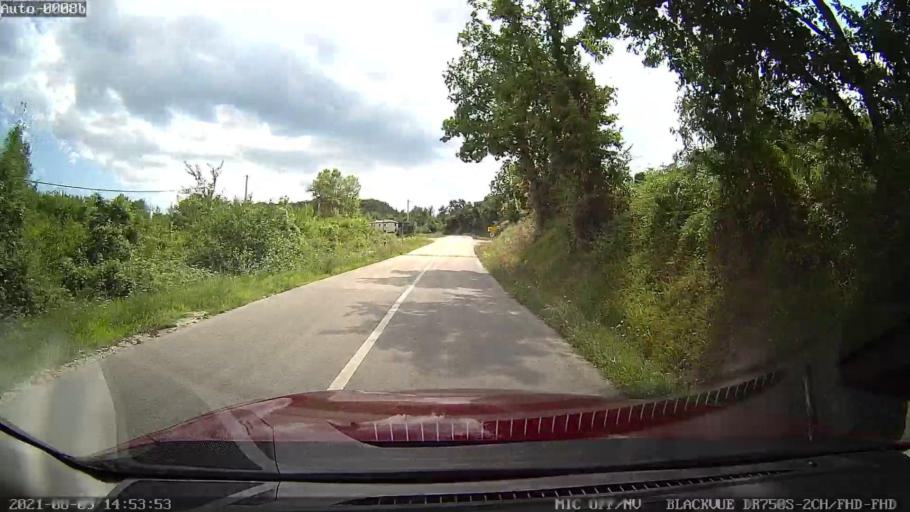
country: HR
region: Istarska
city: Pazin
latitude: 45.2817
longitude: 14.0758
